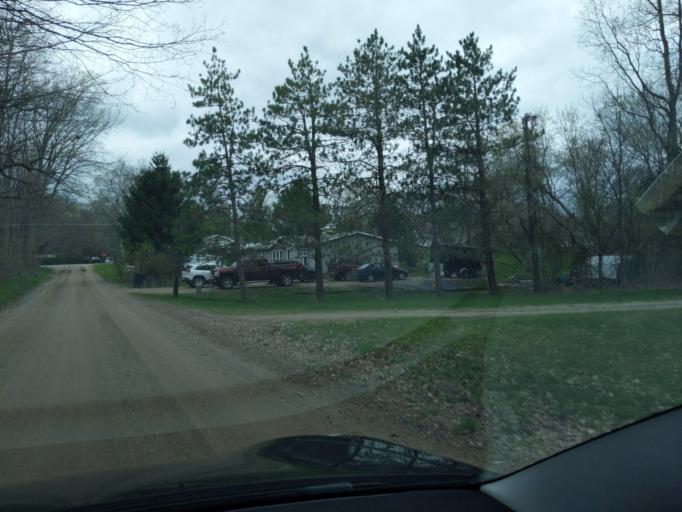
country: US
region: Michigan
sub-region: Ingham County
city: Stockbridge
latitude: 42.4390
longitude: -84.0950
